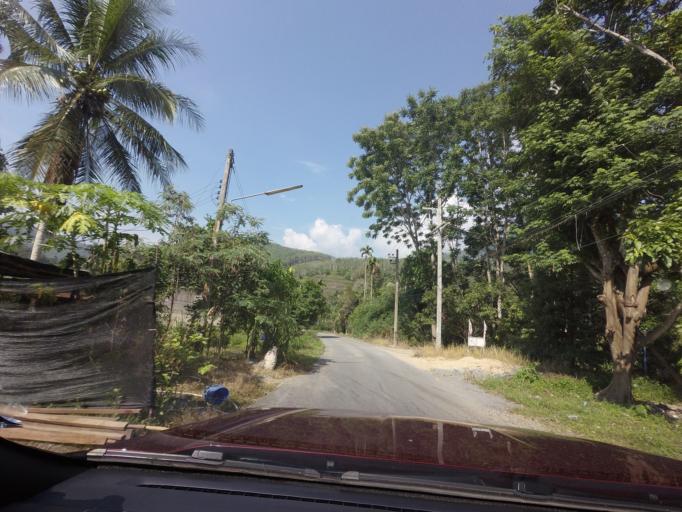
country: TH
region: Yala
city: Than To
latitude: 5.9864
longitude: 101.1986
